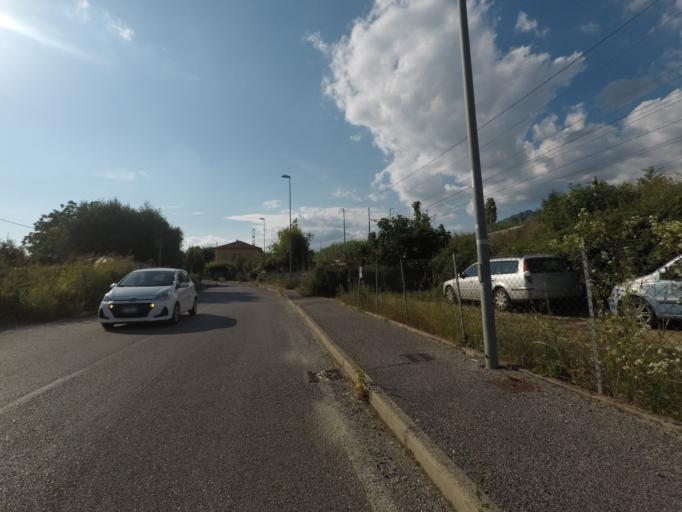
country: IT
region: Tuscany
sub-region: Provincia di Massa-Carrara
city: Capanne-Prato-Cinquale
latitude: 44.0173
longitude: 10.1446
